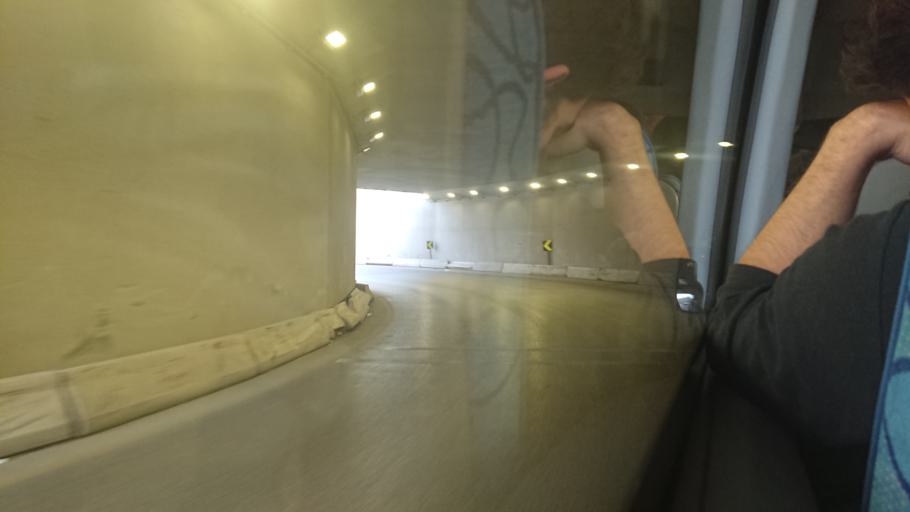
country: TR
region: Ankara
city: Ankara
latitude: 39.9053
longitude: 32.7873
